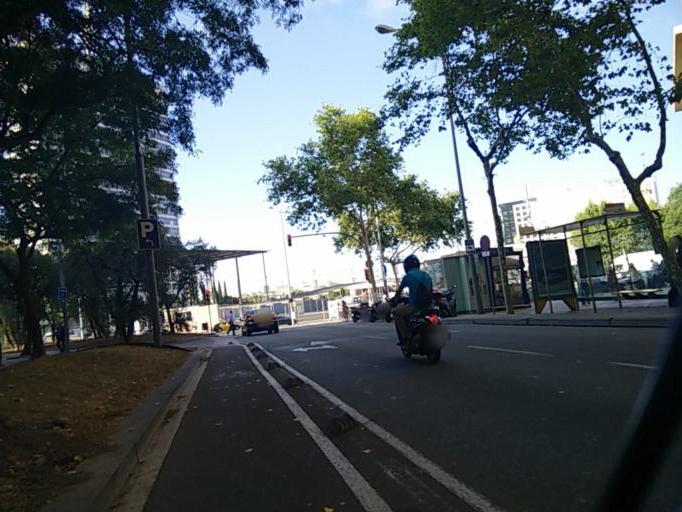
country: ES
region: Catalonia
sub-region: Provincia de Barcelona
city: les Corts
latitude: 41.3813
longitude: 2.1423
